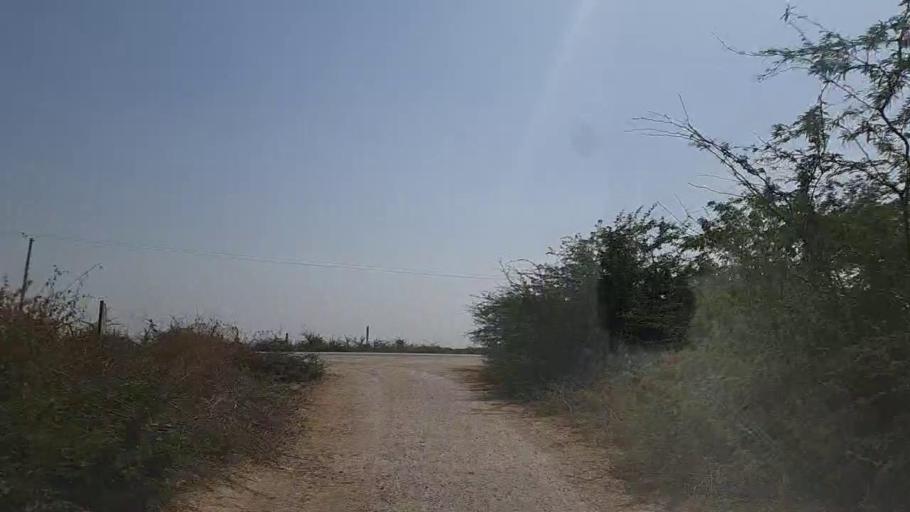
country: PK
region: Sindh
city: Naukot
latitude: 24.6247
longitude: 69.2701
